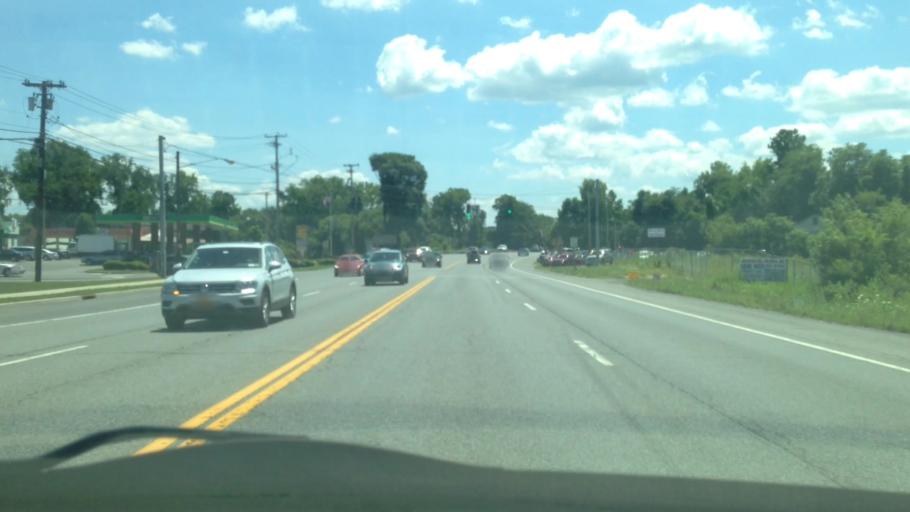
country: US
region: New York
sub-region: Ulster County
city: Kingston
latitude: 41.9415
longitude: -74.0277
